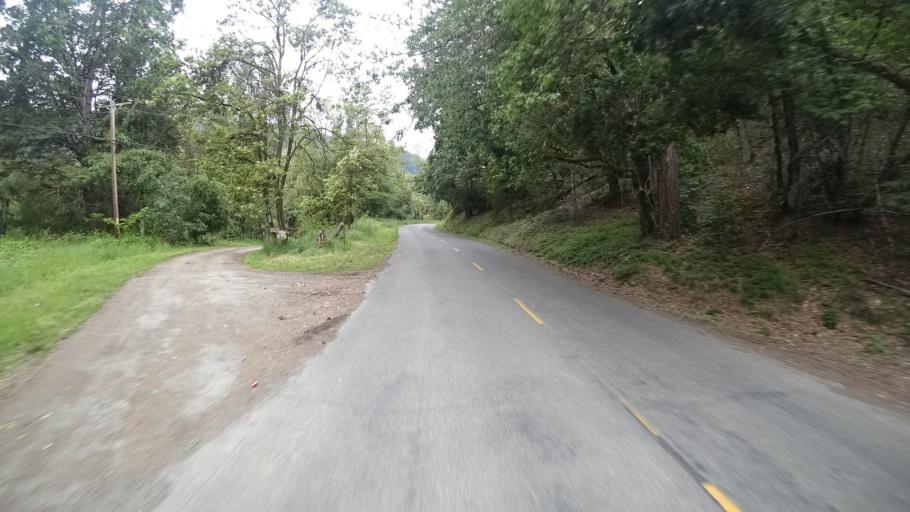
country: US
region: California
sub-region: Humboldt County
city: Willow Creek
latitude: 40.9652
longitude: -123.6339
